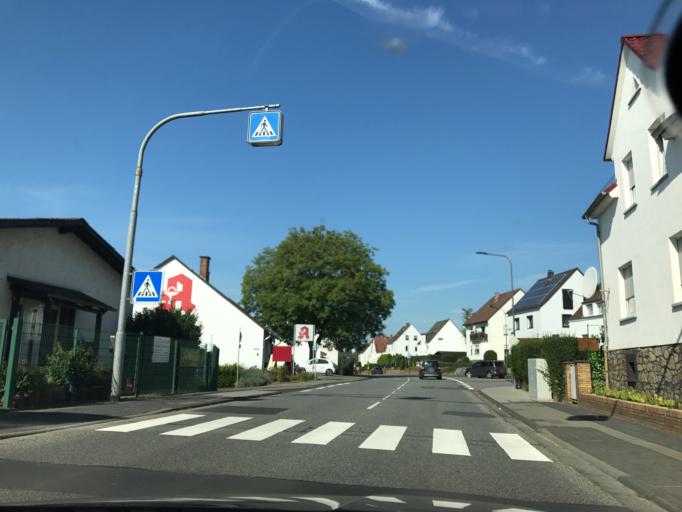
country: DE
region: Hesse
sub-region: Regierungsbezirk Giessen
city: Wetzlar
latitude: 50.5855
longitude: 8.5468
